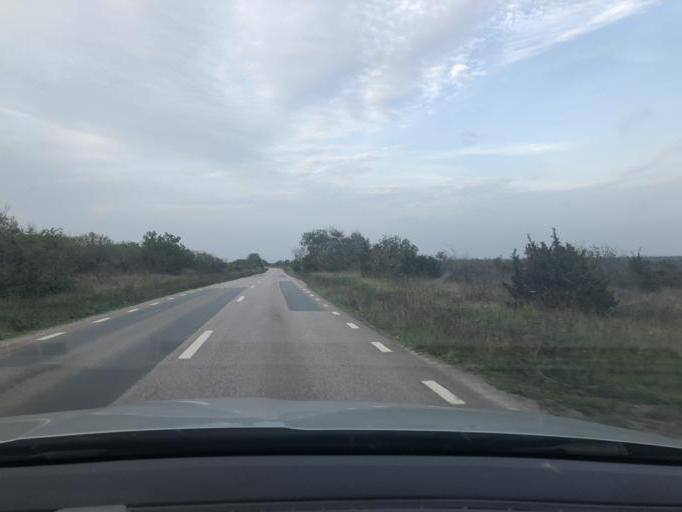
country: SE
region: Kalmar
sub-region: Morbylanga Kommun
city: Moerbylanga
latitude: 56.5622
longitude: 16.4500
